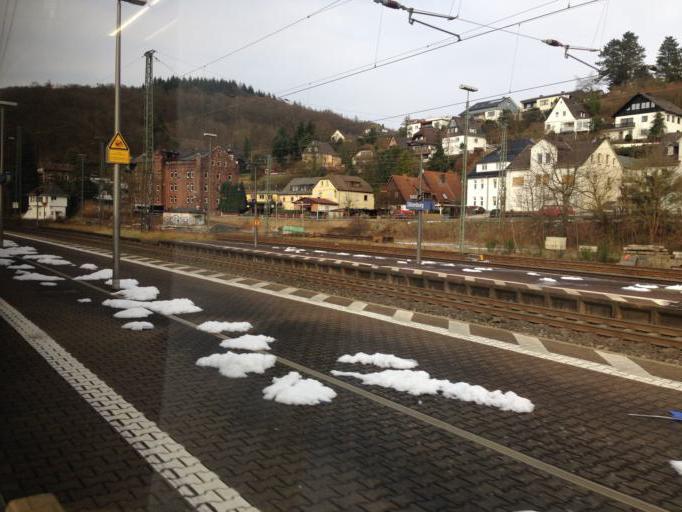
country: DE
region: Hesse
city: Dillenburg
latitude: 50.7358
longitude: 8.2943
